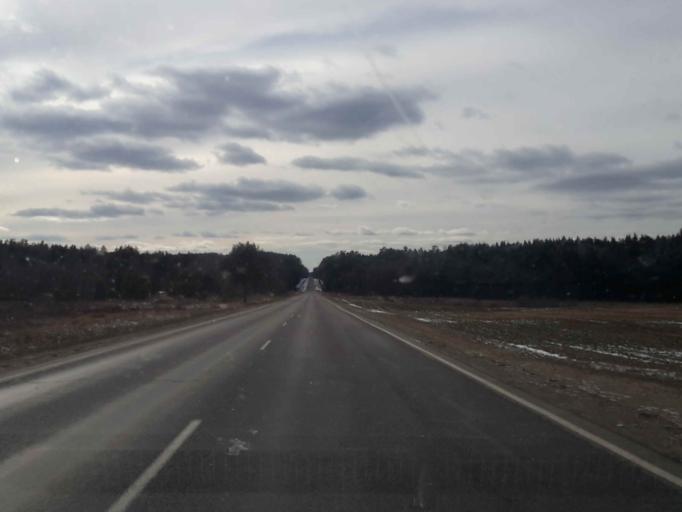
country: BY
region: Vitebsk
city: Pastavy
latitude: 55.0211
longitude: 26.9205
